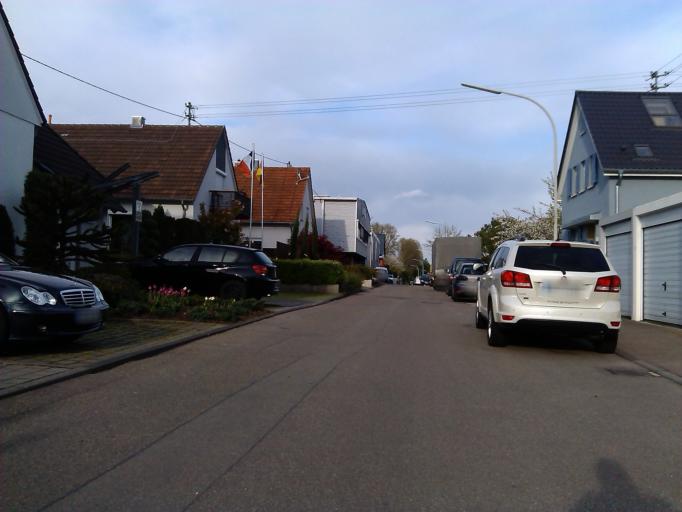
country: DE
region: Baden-Wuerttemberg
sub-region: Regierungsbezirk Stuttgart
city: Talheim
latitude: 49.1177
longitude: 9.1694
